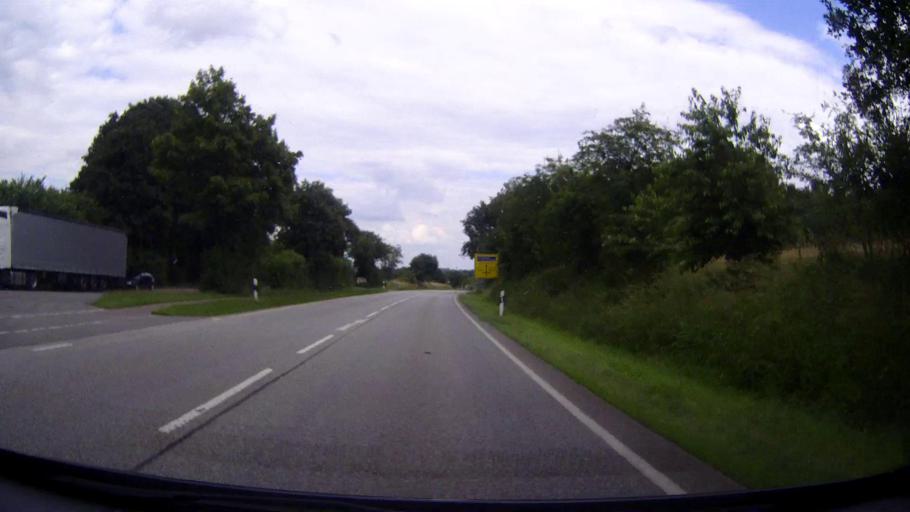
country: DE
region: Schleswig-Holstein
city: Aukrug
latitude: 54.0686
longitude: 9.7813
